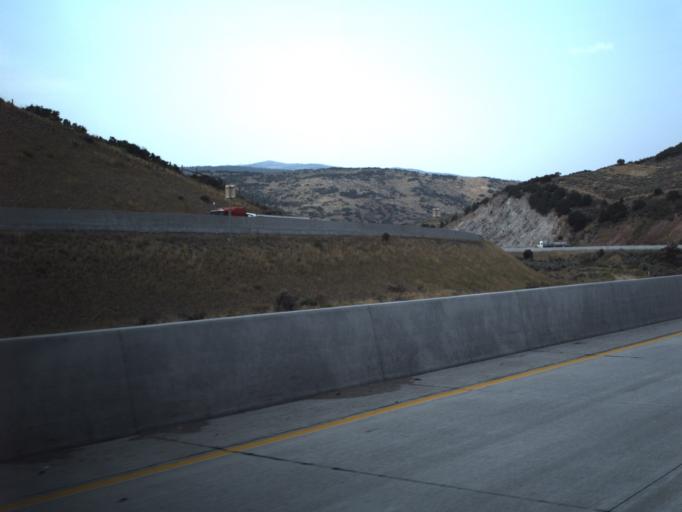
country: US
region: Utah
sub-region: Summit County
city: Snyderville
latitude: 40.7656
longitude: -111.4695
